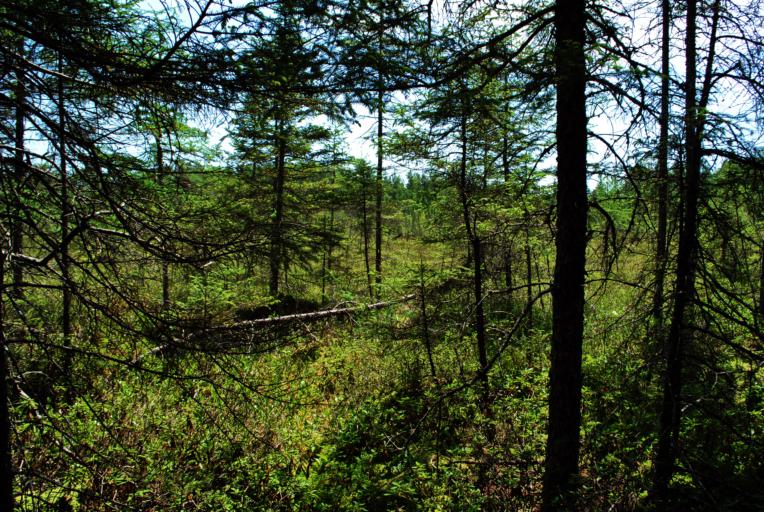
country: US
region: Wisconsin
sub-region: Sawyer County
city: Hayward
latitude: 46.0132
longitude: -91.5338
